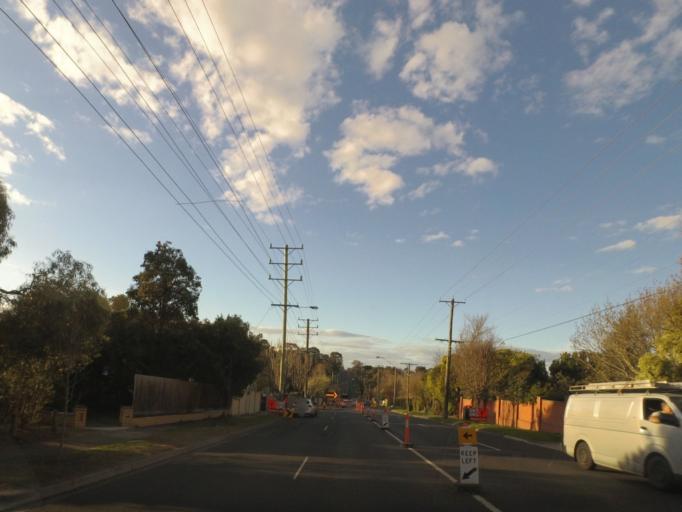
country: AU
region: Victoria
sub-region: Whitehorse
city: Surrey Hills
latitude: -37.8328
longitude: 145.0987
